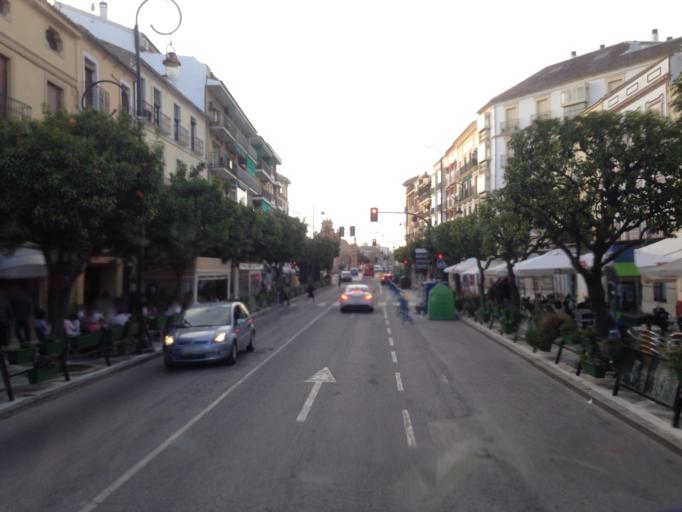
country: ES
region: Andalusia
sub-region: Provincia de Malaga
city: Antequera
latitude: 37.0209
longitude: -4.5642
